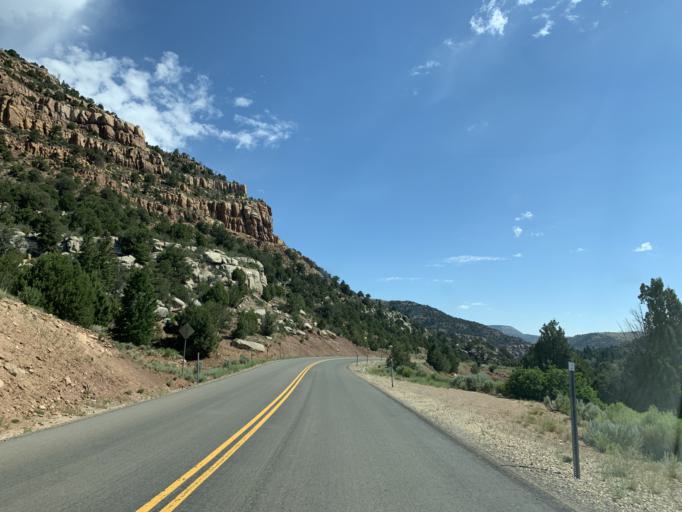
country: US
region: Utah
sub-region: Carbon County
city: East Carbon City
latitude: 39.7447
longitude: -110.5572
